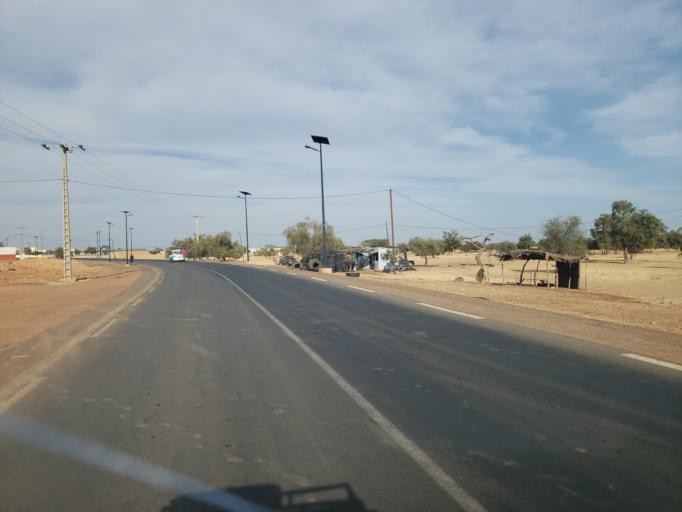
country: SN
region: Matam
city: Ranerou
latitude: 15.2944
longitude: -13.9585
